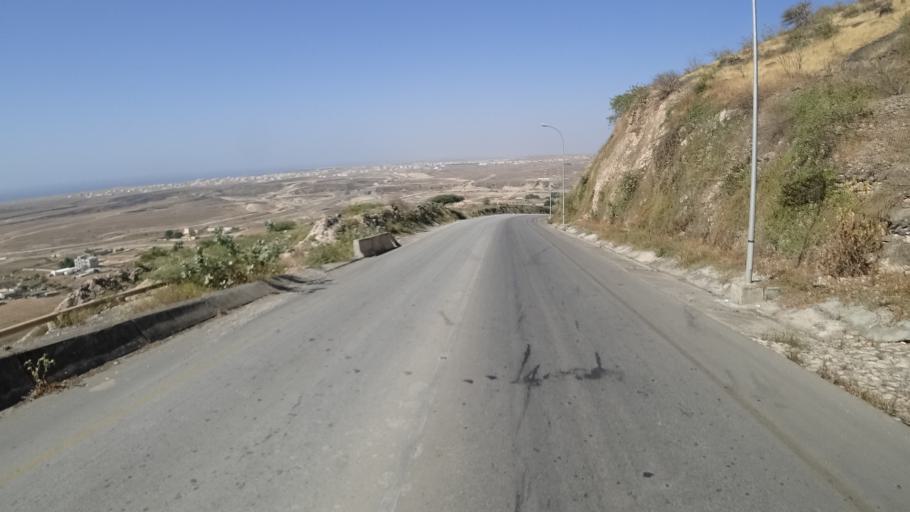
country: OM
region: Zufar
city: Salalah
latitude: 17.0650
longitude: 54.4457
